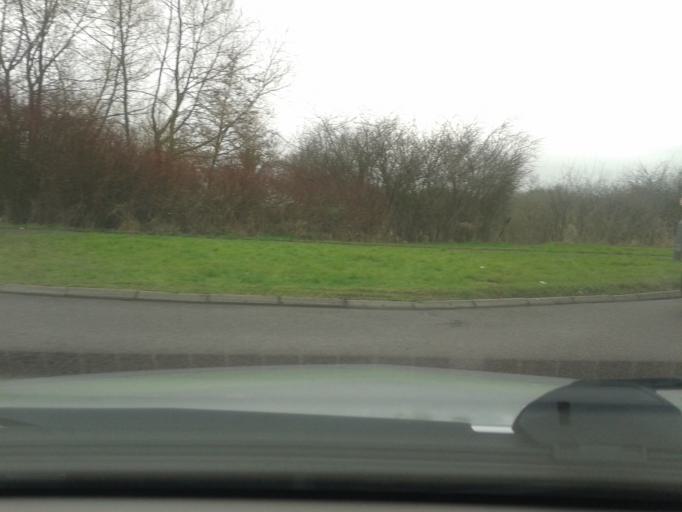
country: GB
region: England
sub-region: South Gloucestershire
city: Yate
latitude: 51.5509
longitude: -2.4260
